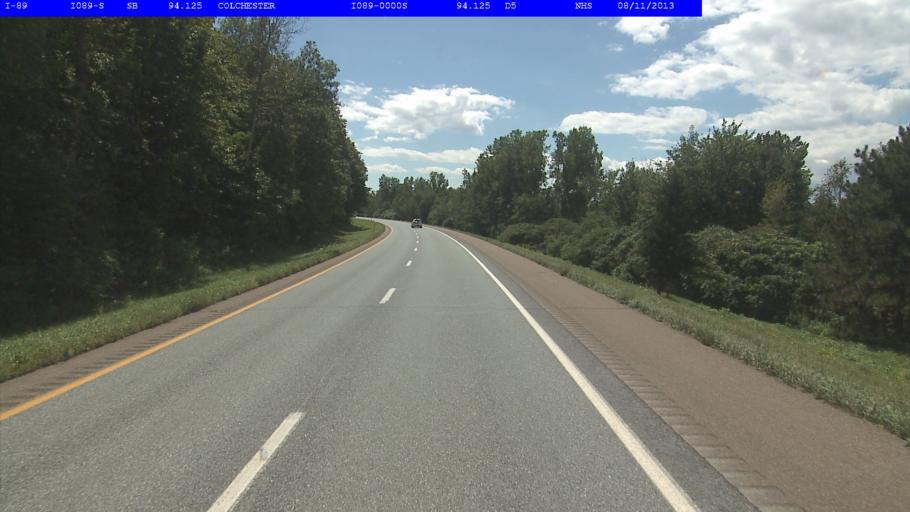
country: US
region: Vermont
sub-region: Chittenden County
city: Winooski
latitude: 44.5402
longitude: -73.1990
